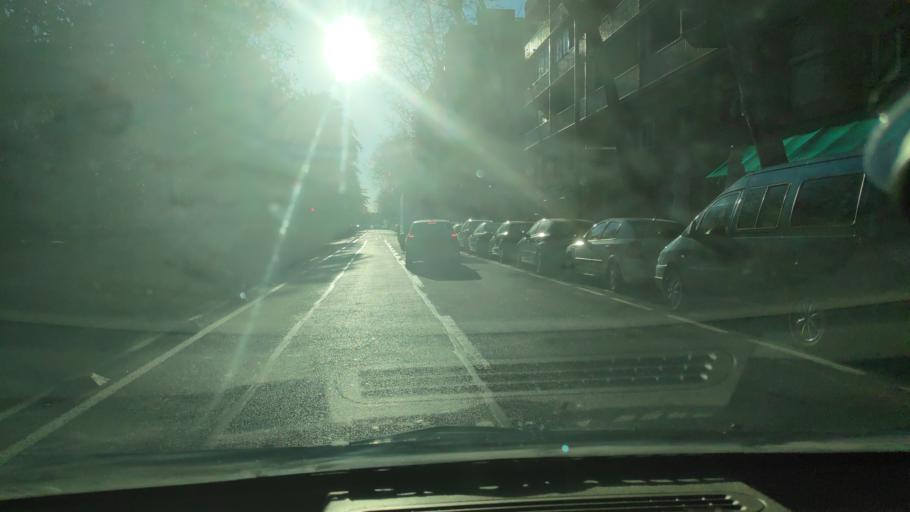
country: ES
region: Catalonia
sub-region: Provincia de Barcelona
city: Sant Marti
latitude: 41.4138
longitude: 2.2156
